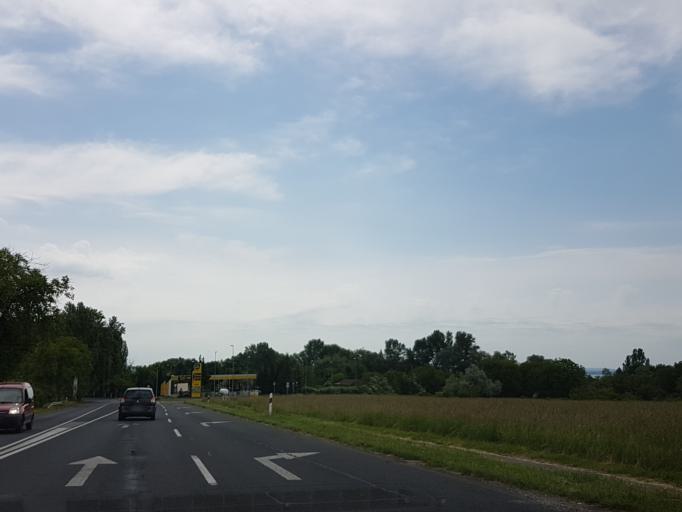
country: HU
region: Veszprem
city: Revfueloep
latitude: 46.8275
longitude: 17.6032
